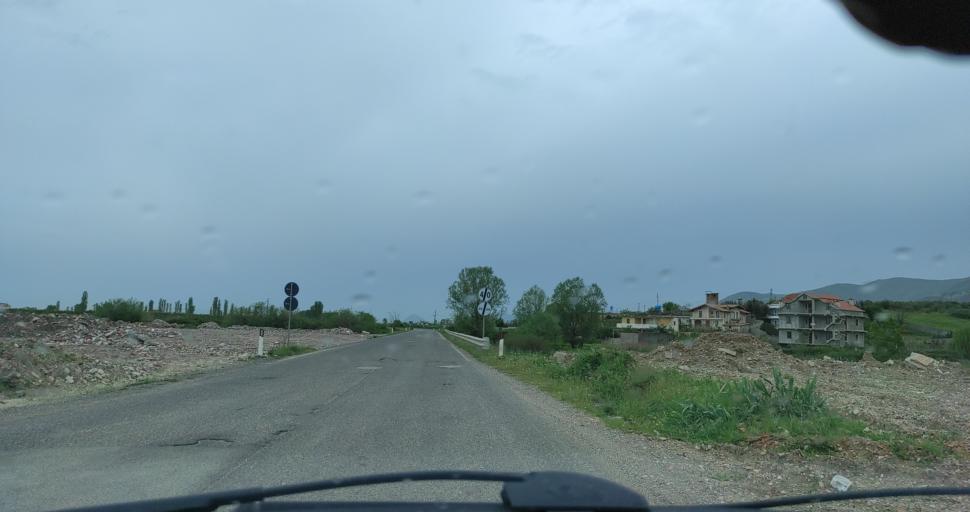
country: AL
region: Lezhe
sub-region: Rrethi i Kurbinit
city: Mamurras
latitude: 41.5928
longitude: 19.6990
